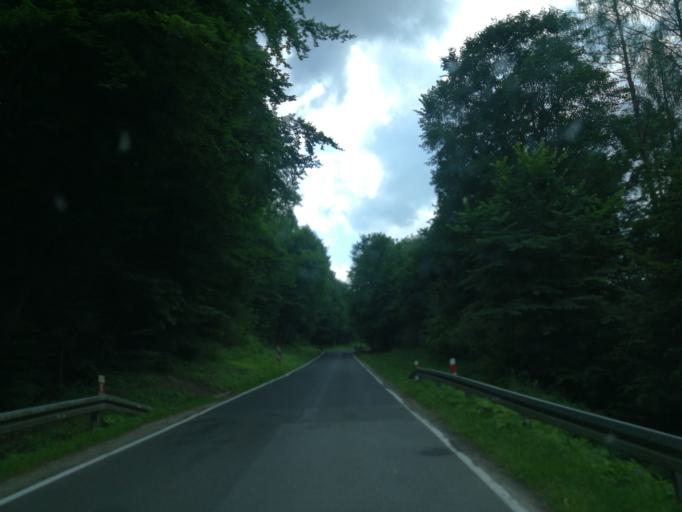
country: PL
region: Subcarpathian Voivodeship
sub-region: Powiat leski
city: Polanczyk
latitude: 49.3981
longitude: 22.4406
